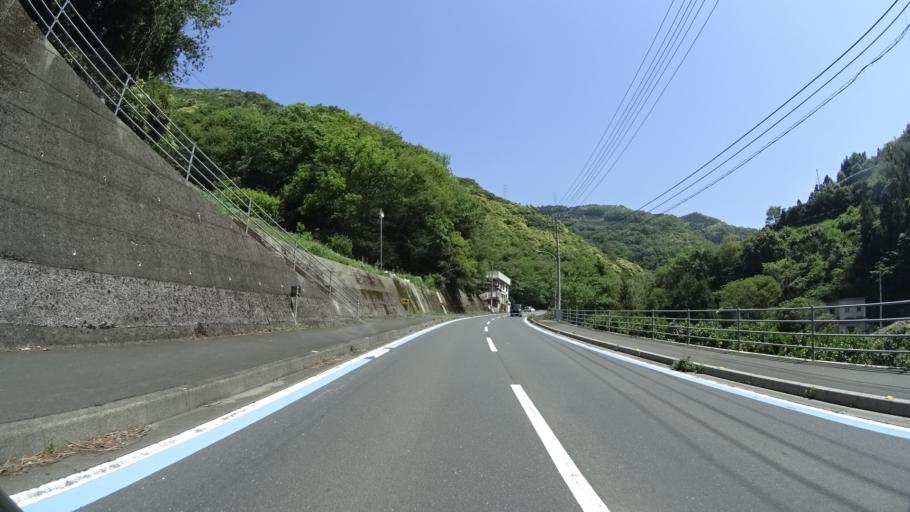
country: JP
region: Ehime
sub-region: Nishiuwa-gun
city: Ikata-cho
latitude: 33.4959
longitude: 132.3677
